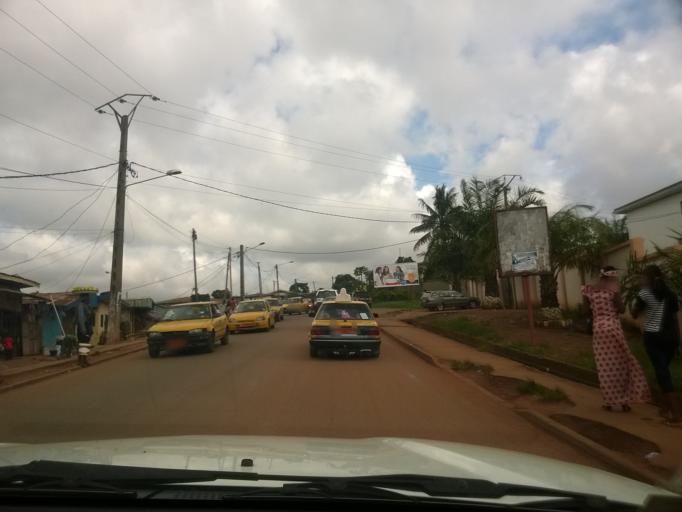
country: CM
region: Centre
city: Yaounde
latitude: 3.8652
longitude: 11.5344
